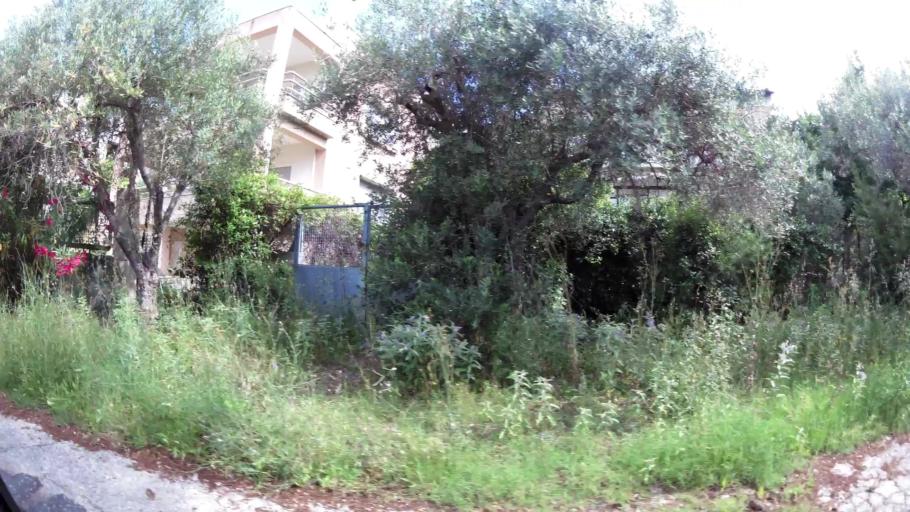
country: GR
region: Central Macedonia
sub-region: Nomos Thessalonikis
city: Panorama
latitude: 40.5798
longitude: 23.0088
